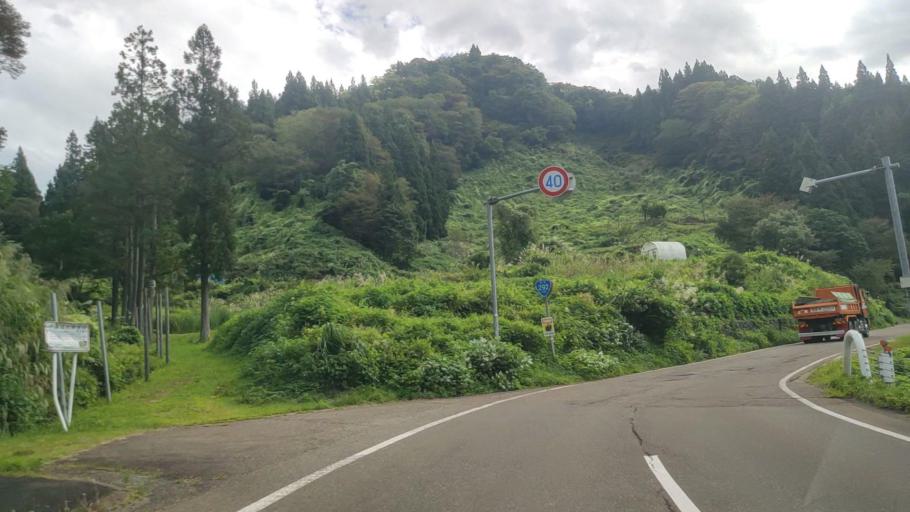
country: JP
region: Niigata
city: Arai
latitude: 36.9345
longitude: 138.2968
